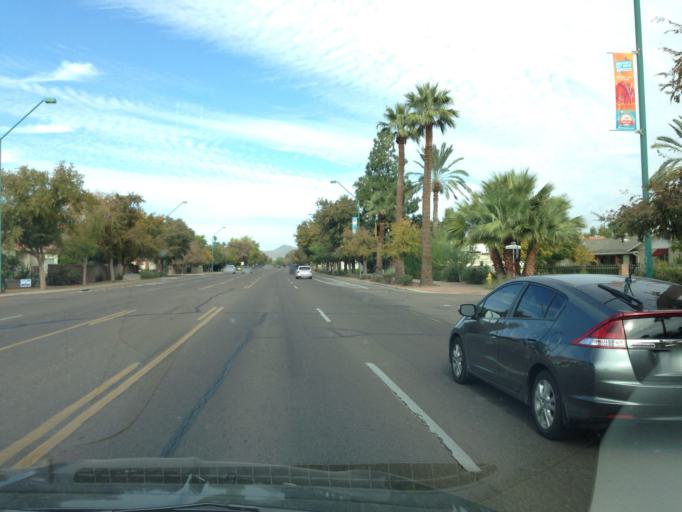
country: US
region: Arizona
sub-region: Maricopa County
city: Phoenix
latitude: 33.5176
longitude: -112.0737
